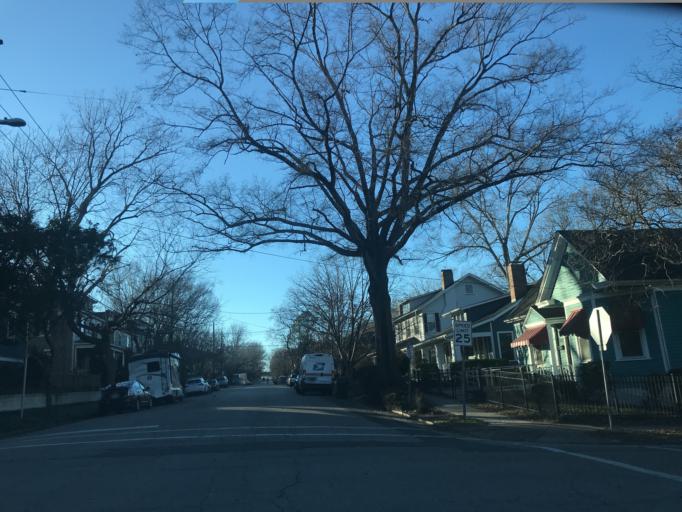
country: US
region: North Carolina
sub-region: Wake County
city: Raleigh
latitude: 35.7835
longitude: -78.6293
